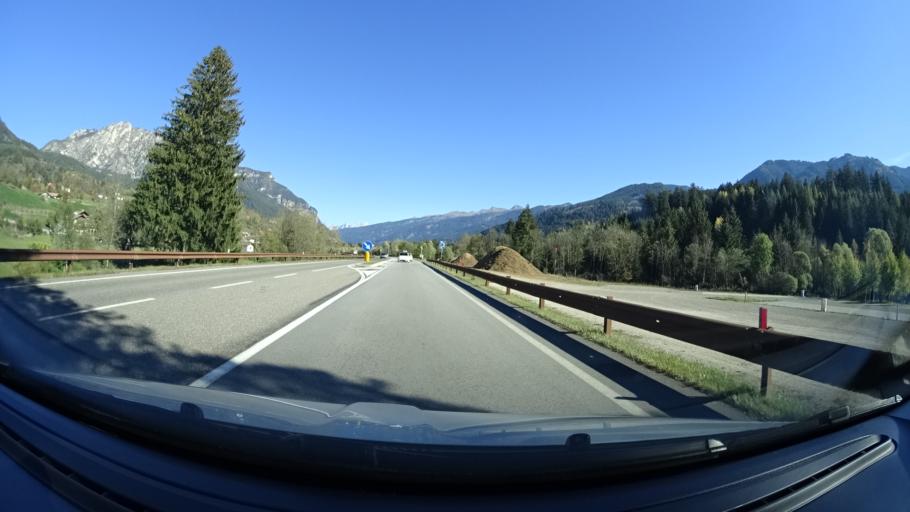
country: IT
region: Trentino-Alto Adige
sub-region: Provincia di Trento
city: Cavalese
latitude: 46.2845
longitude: 11.4722
